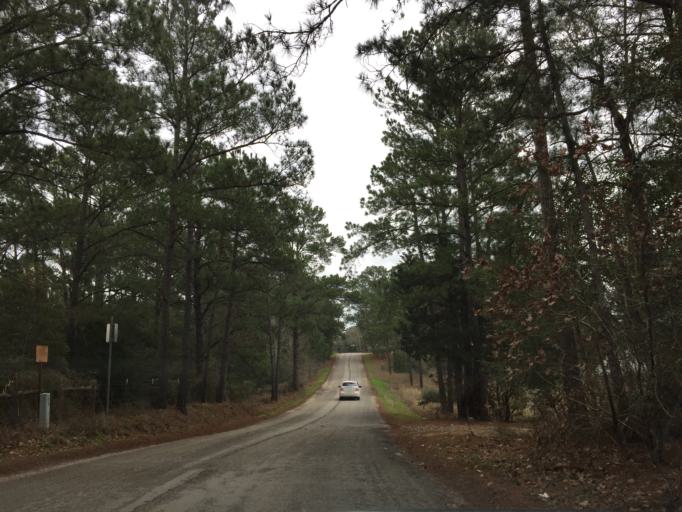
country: US
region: Texas
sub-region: Bastrop County
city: Bastrop
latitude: 30.1267
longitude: -97.2963
